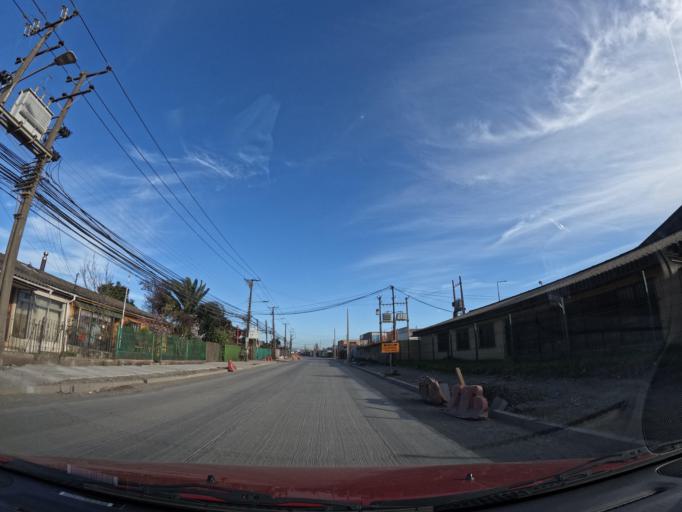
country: CL
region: Biobio
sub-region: Provincia de Concepcion
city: Talcahuano
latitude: -36.7610
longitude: -73.0811
